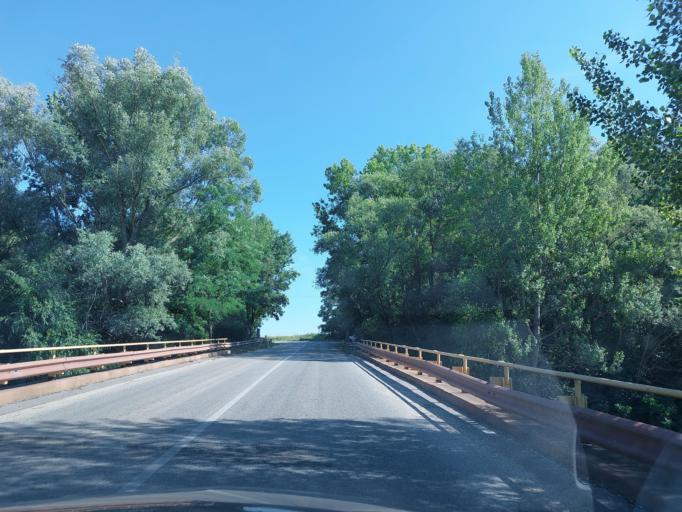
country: HU
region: Veszprem
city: Ajka
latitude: 47.0829
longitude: 17.5222
